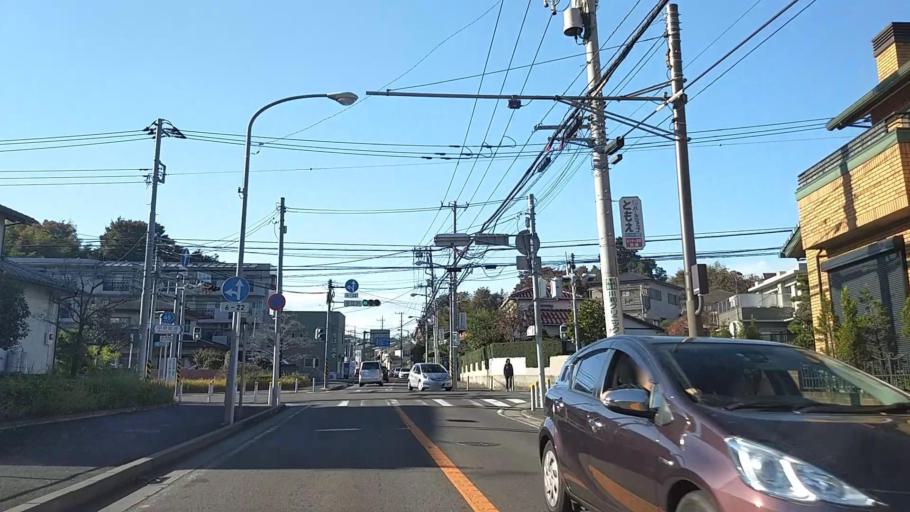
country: JP
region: Kanagawa
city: Yokohama
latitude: 35.5192
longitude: 139.5606
